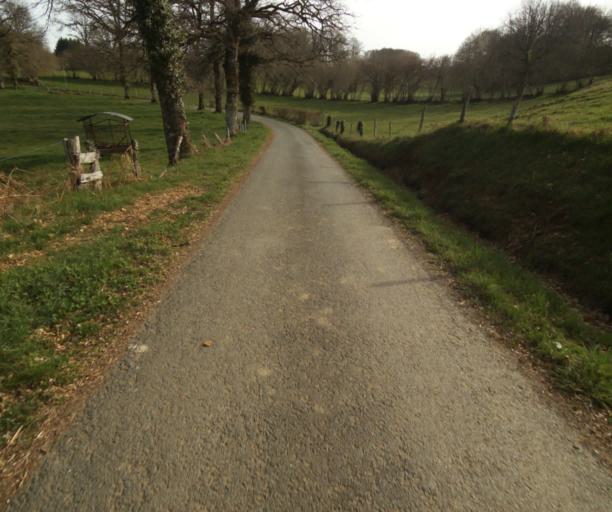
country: FR
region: Limousin
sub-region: Departement de la Correze
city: Chamboulive
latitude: 45.4227
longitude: 1.7617
